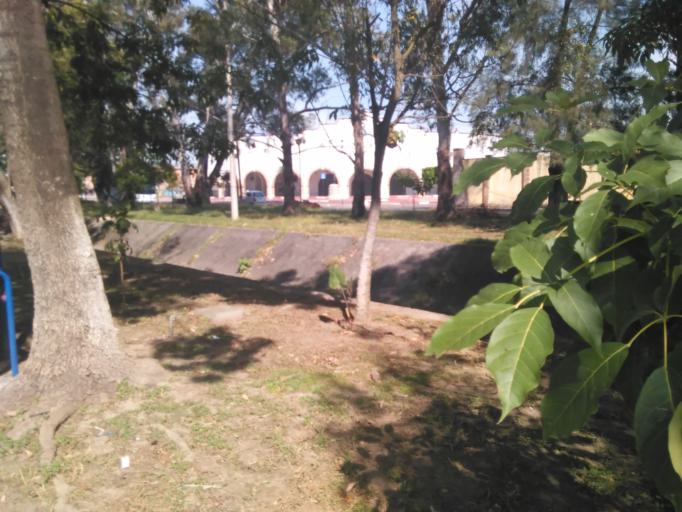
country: MX
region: Nayarit
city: Tepic
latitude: 21.4896
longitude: -104.8814
